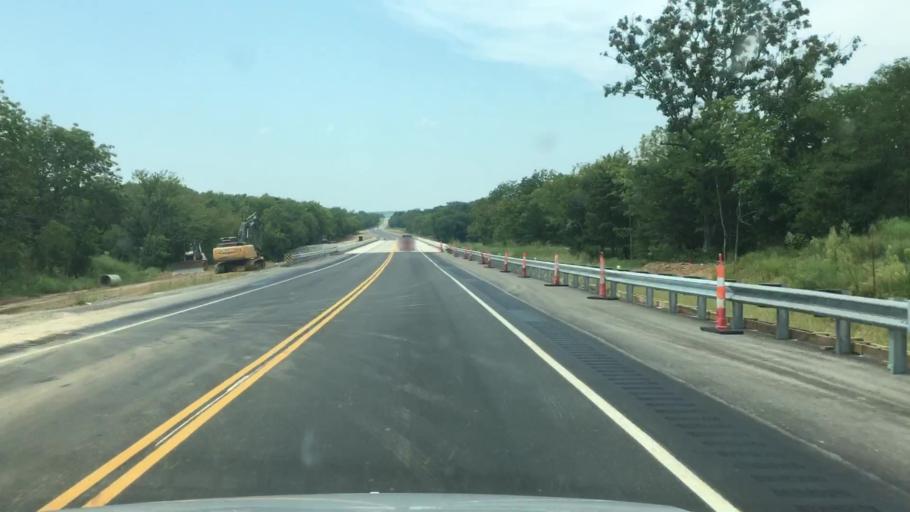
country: US
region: Oklahoma
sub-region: Muskogee County
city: Fort Gibson
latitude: 35.9370
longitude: -95.1748
